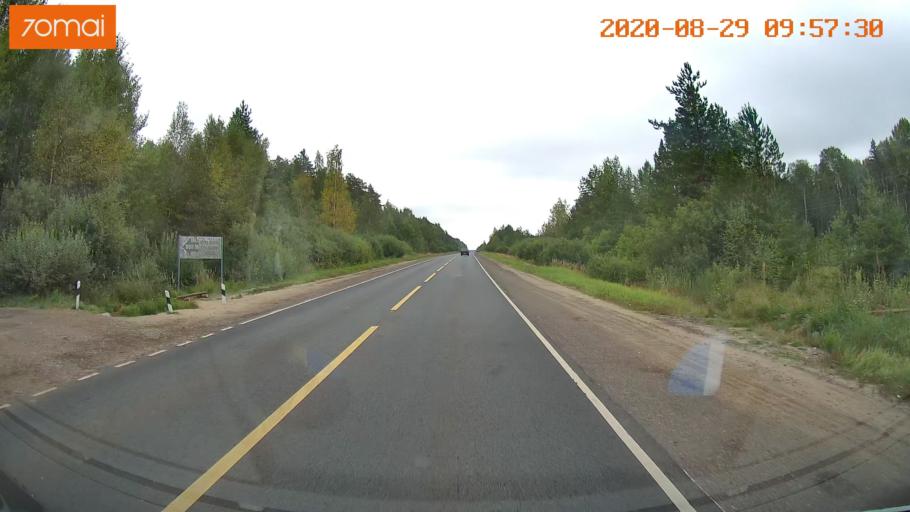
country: RU
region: Ivanovo
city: Zarechnyy
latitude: 57.4162
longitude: 42.3157
